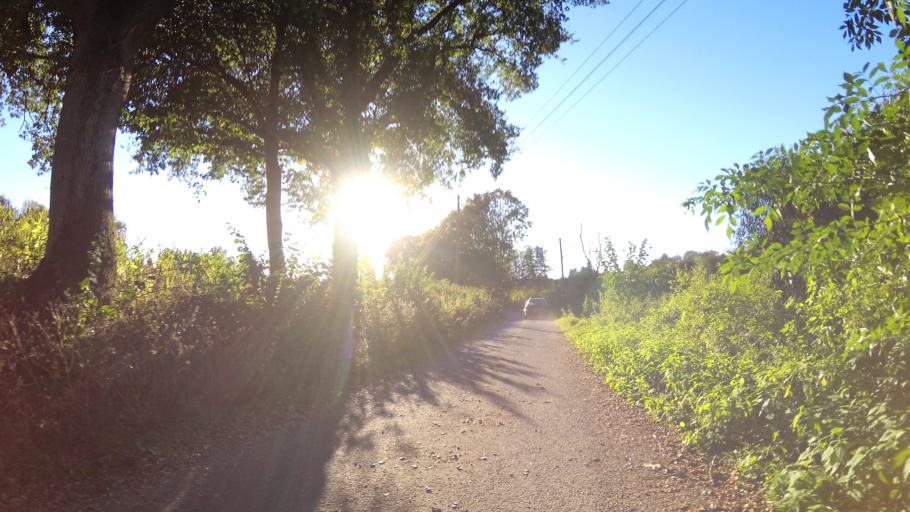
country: DE
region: Saarland
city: Ottweiler
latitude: 49.4315
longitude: 7.1770
